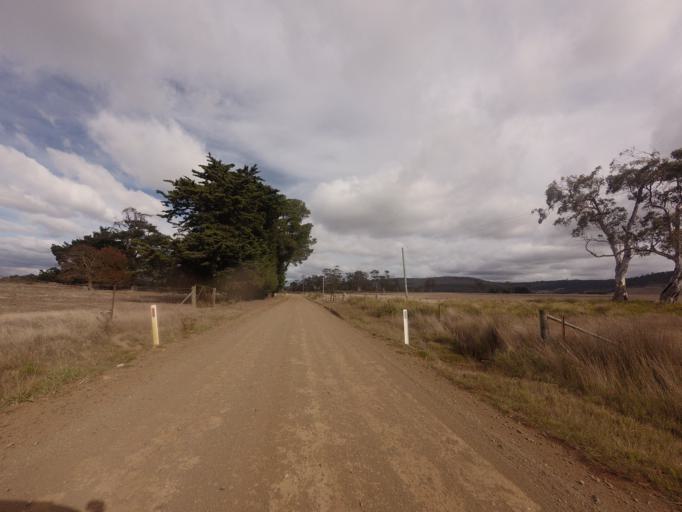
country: AU
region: Tasmania
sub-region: Brighton
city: Bridgewater
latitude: -42.4349
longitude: 147.3860
